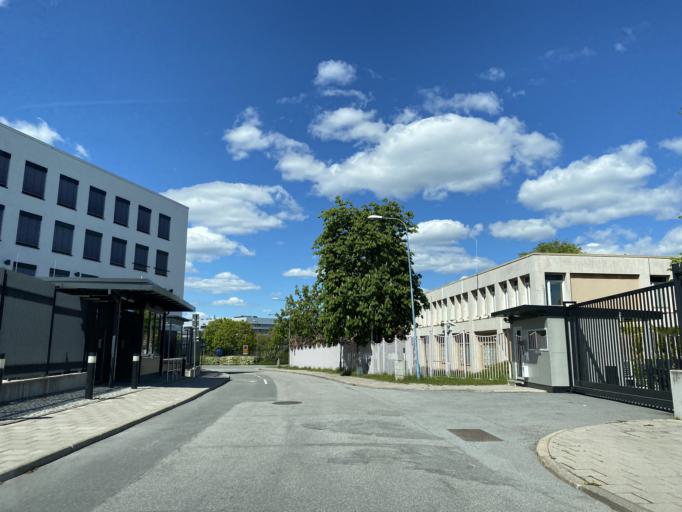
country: SE
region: Stockholm
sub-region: Stockholms Kommun
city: OEstermalm
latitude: 59.3342
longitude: 18.1069
